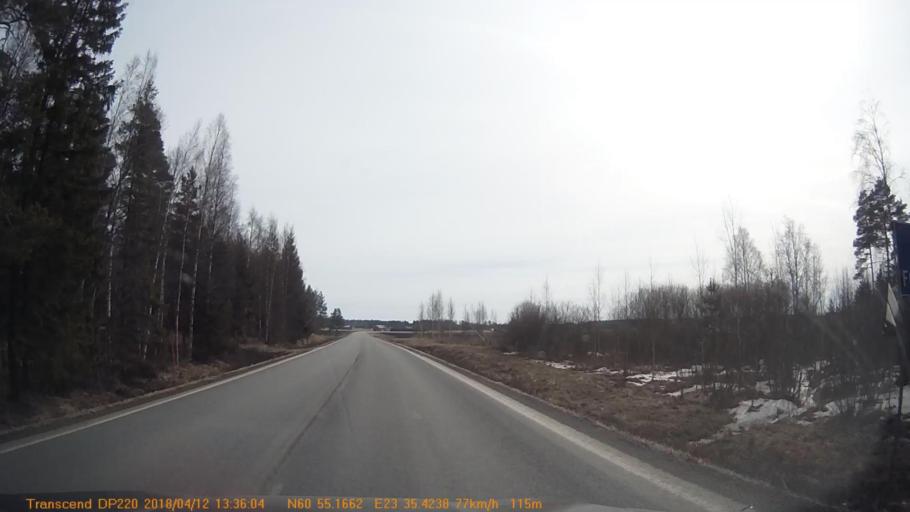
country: FI
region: Haeme
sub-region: Forssa
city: Forssa
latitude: 60.9191
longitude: 23.5907
